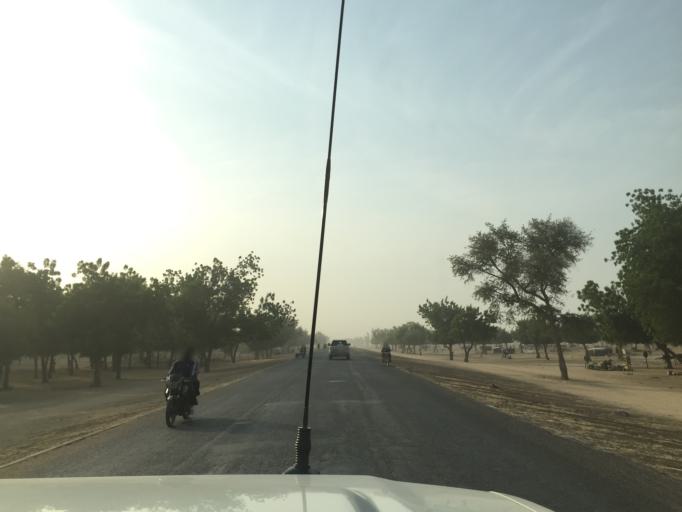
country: CM
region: Far North
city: Kousseri
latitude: 12.0564
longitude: 15.1061
